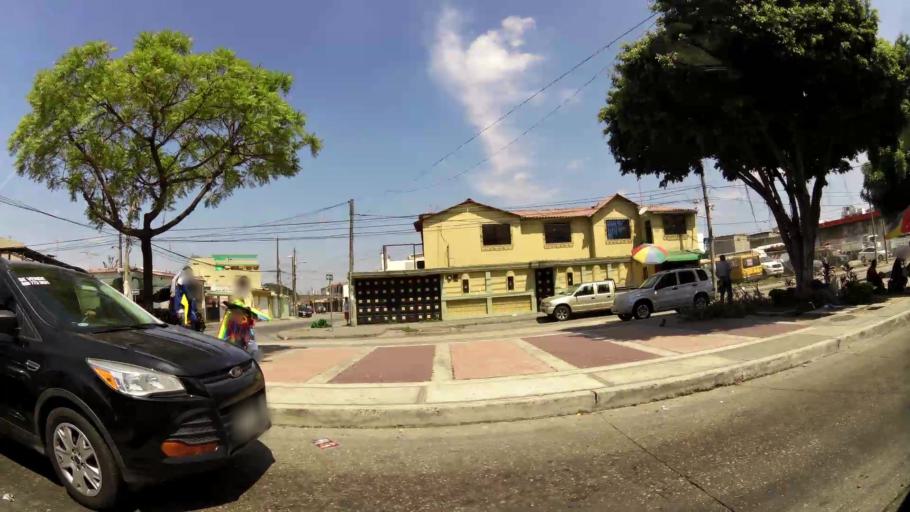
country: EC
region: Guayas
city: Eloy Alfaro
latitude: -2.1207
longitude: -79.9044
